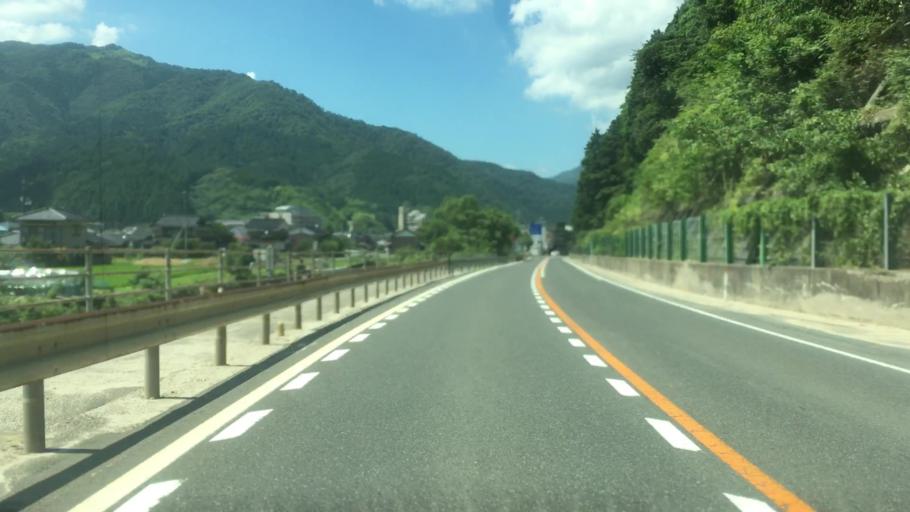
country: JP
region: Tottori
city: Tottori
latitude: 35.2580
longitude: 134.2280
